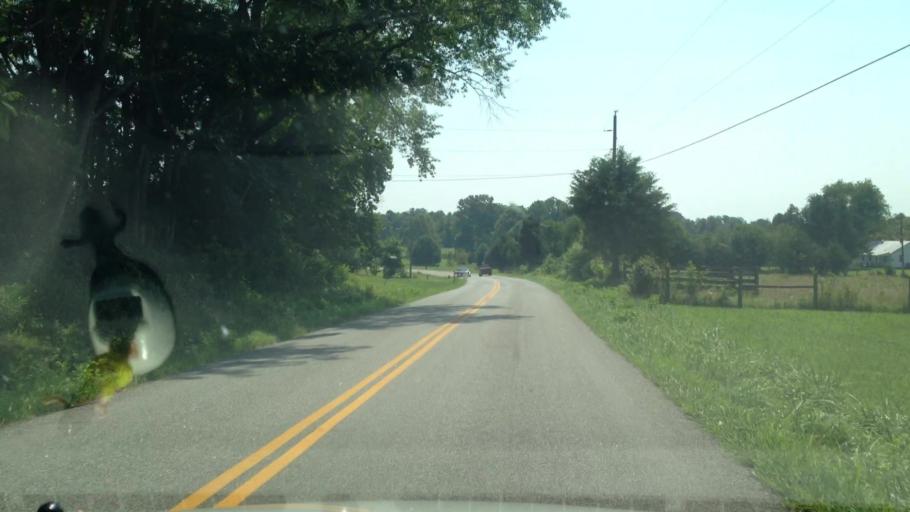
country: US
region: Virginia
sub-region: Patrick County
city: Stuart
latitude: 36.5783
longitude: -80.2526
